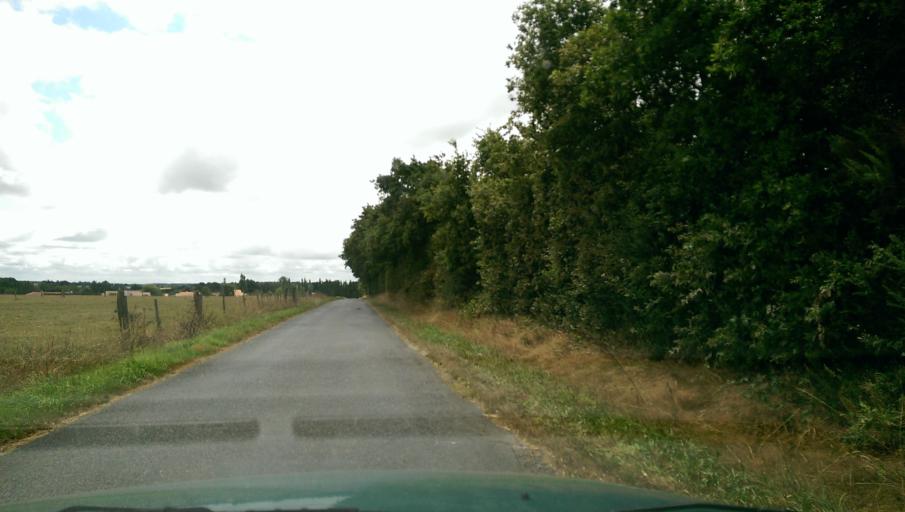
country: FR
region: Pays de la Loire
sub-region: Departement de la Loire-Atlantique
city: Remouille
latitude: 47.0626
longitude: -1.3632
